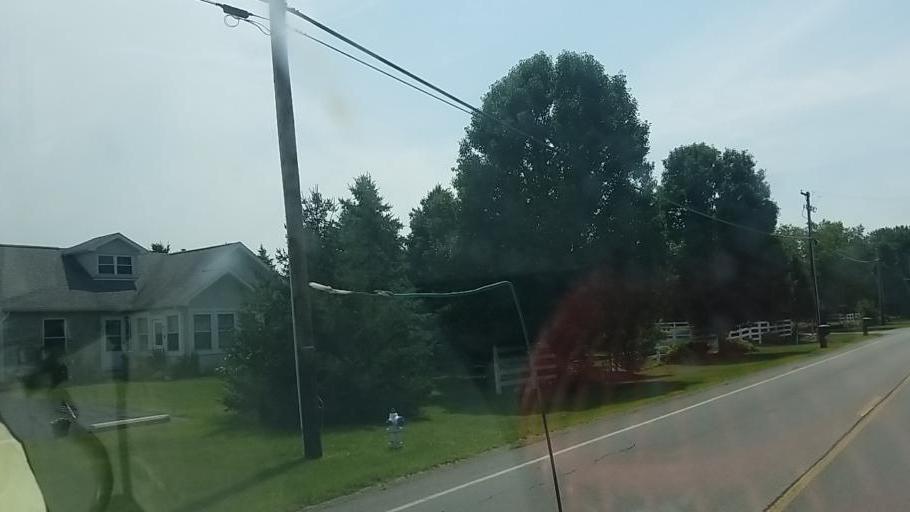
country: US
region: Ohio
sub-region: Marion County
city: Marion
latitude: 40.5886
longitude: -83.0736
